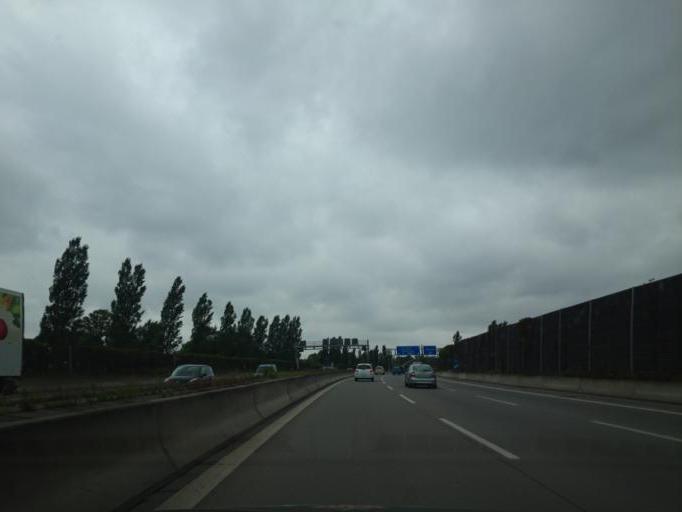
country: DE
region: Berlin
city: Buckow
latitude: 52.4499
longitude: 13.4652
